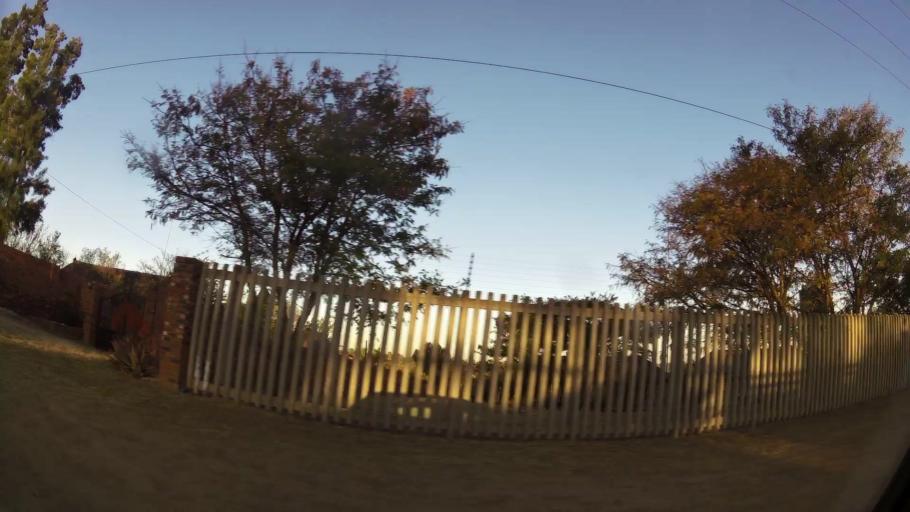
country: ZA
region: Gauteng
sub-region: City of Johannesburg Metropolitan Municipality
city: Diepsloot
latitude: -25.9427
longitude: 28.0535
